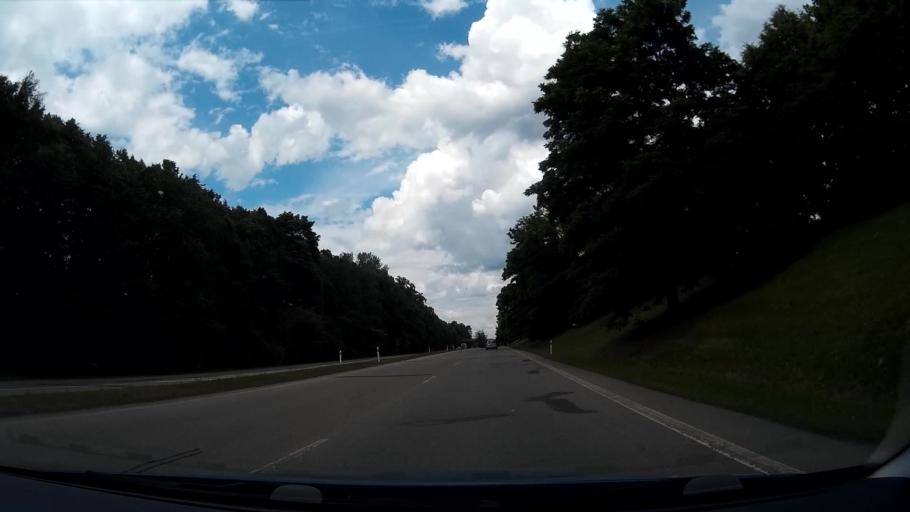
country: CZ
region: South Moravian
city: Troubsko
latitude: 49.2173
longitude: 16.5216
